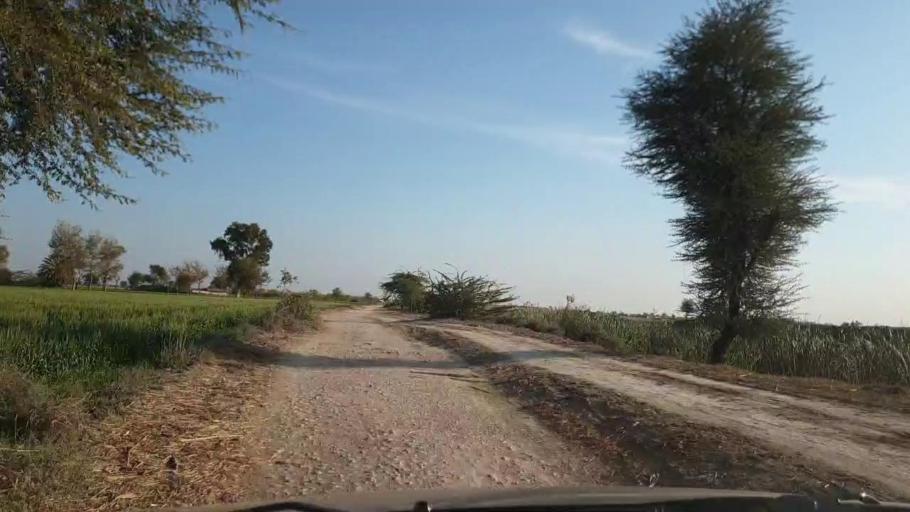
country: PK
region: Sindh
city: Khadro
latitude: 26.2134
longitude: 68.7428
